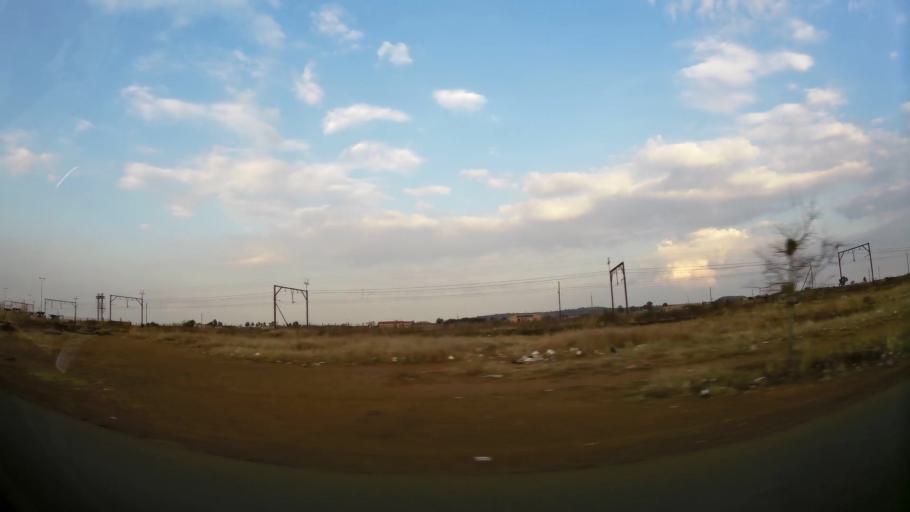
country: ZA
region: Gauteng
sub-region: City of Johannesburg Metropolitan Municipality
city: Orange Farm
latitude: -26.5679
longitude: 27.8614
